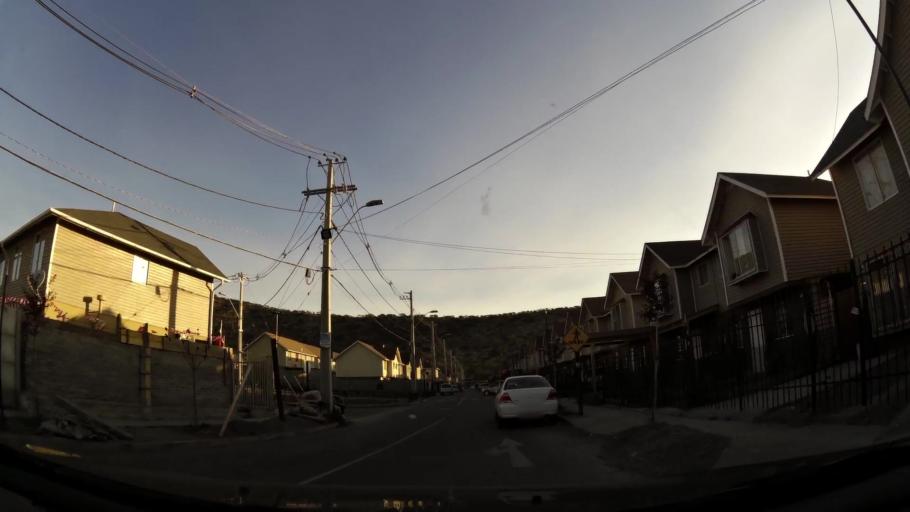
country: CL
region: Santiago Metropolitan
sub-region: Provincia de Cordillera
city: Puente Alto
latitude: -33.6005
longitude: -70.5473
